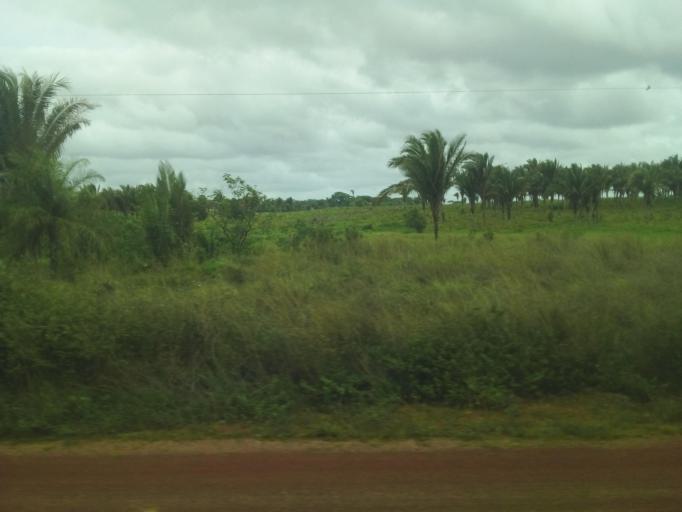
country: BR
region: Maranhao
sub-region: Itapecuru Mirim
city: Itapecuru Mirim
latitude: -3.2150
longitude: -44.4016
